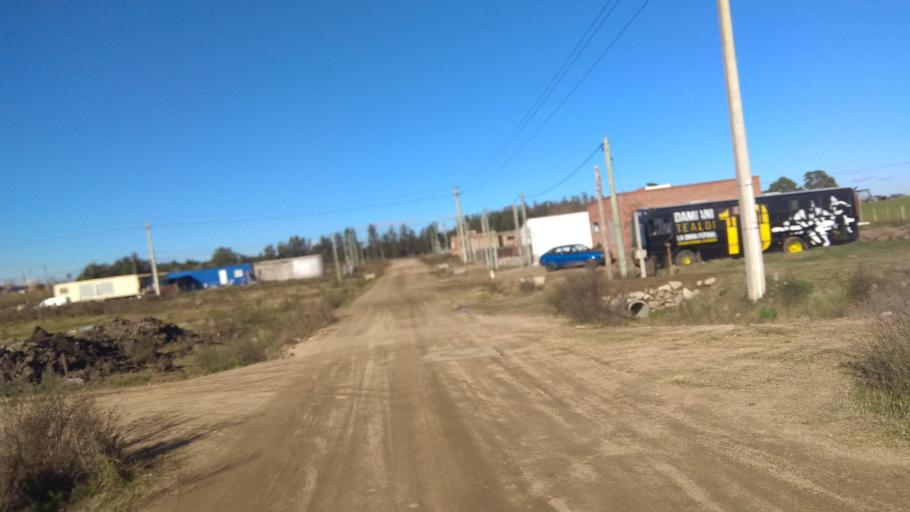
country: UY
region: Florida
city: Florida
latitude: -34.0828
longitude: -56.2409
